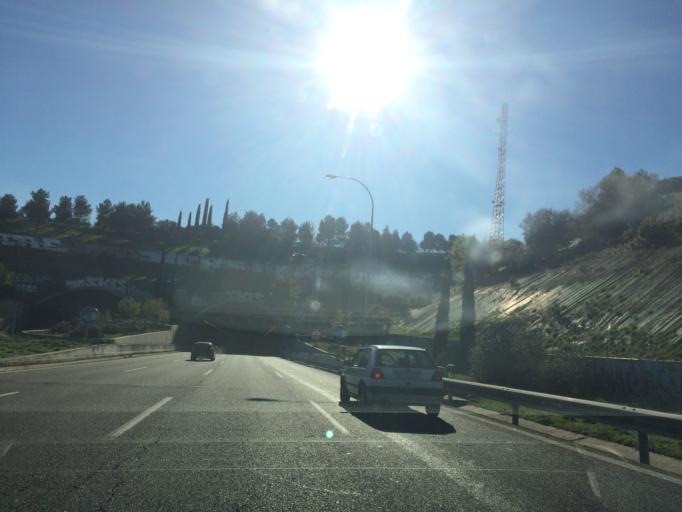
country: ES
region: Madrid
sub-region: Provincia de Madrid
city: Fuencarral-El Pardo
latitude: 40.4873
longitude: -3.7417
